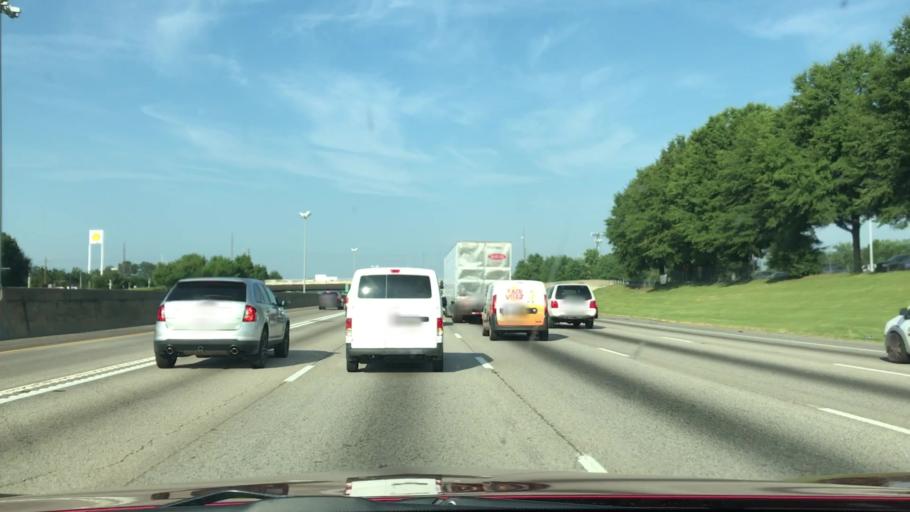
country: US
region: Georgia
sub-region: Gwinnett County
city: Norcross
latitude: 33.9303
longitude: -84.1735
